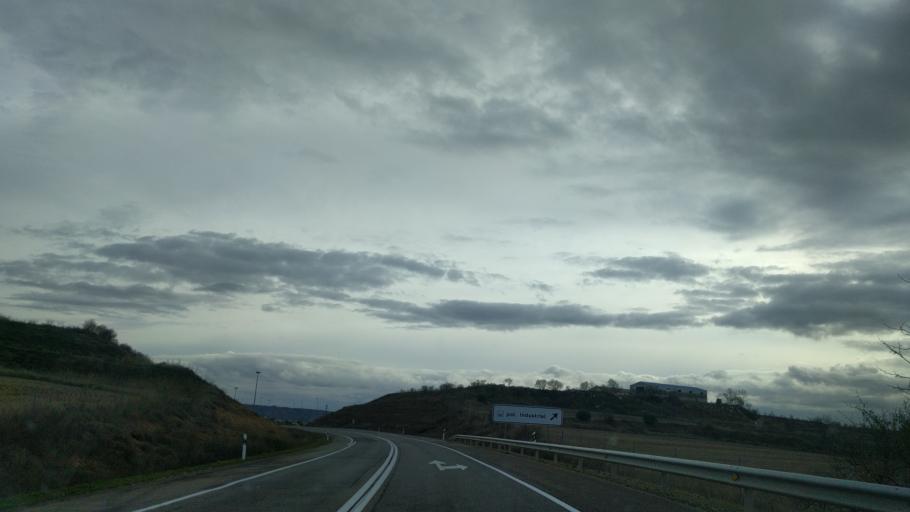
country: ES
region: Aragon
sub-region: Provincia de Huesca
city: Huesca
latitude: 42.1545
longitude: -0.3993
